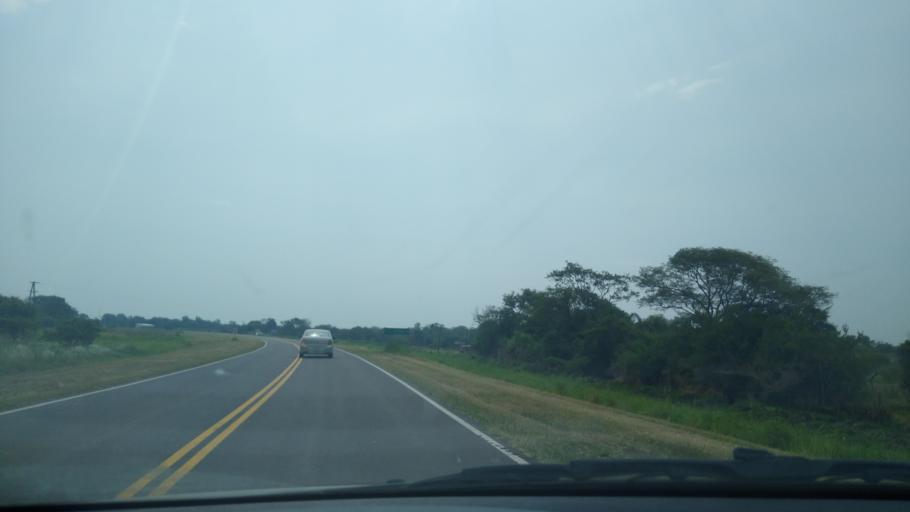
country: AR
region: Chaco
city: La Eduvigis
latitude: -26.8419
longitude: -59.0543
